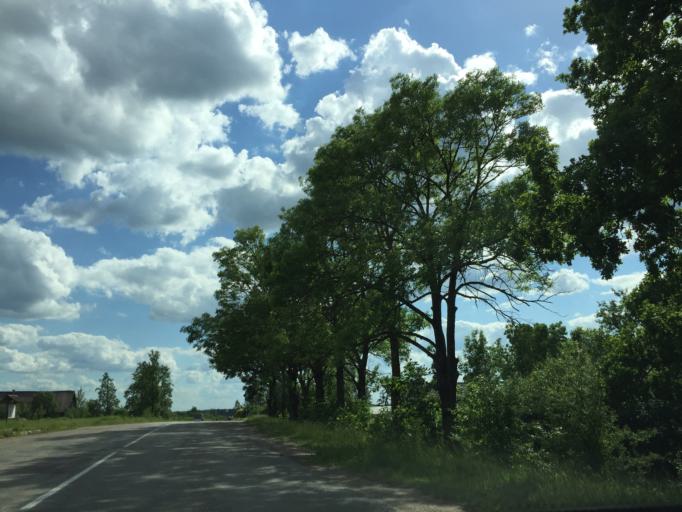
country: LV
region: Jaunpils
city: Jaunpils
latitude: 56.8411
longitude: 23.0398
